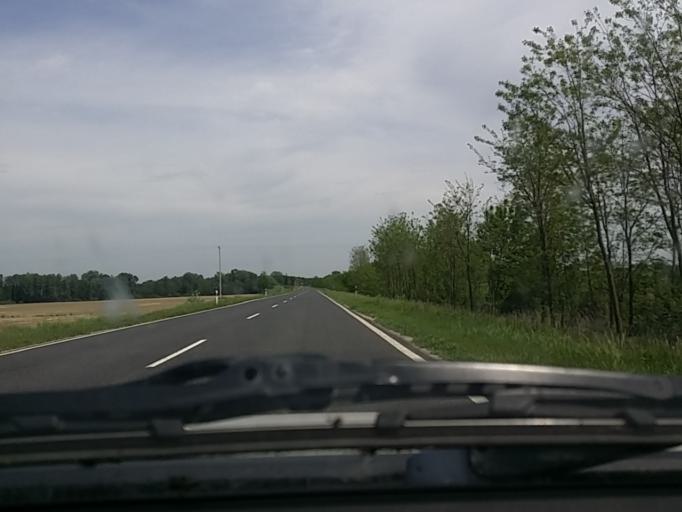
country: HU
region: Somogy
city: Barcs
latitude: 45.9548
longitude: 17.4766
